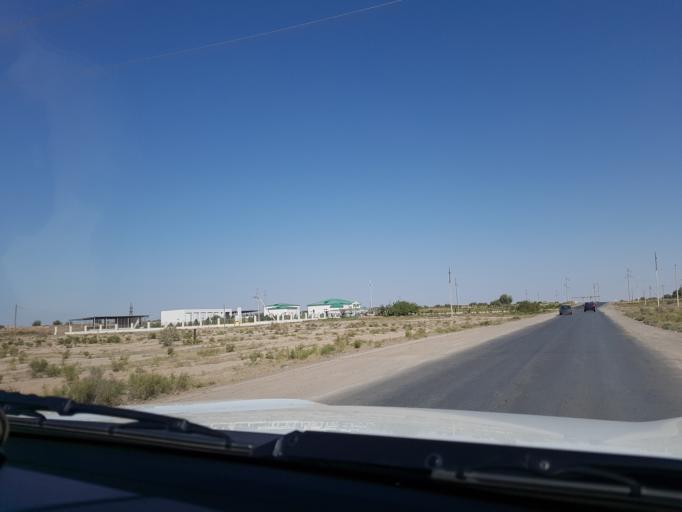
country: IR
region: Razavi Khorasan
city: Sarakhs
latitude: 36.5240
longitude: 61.2322
